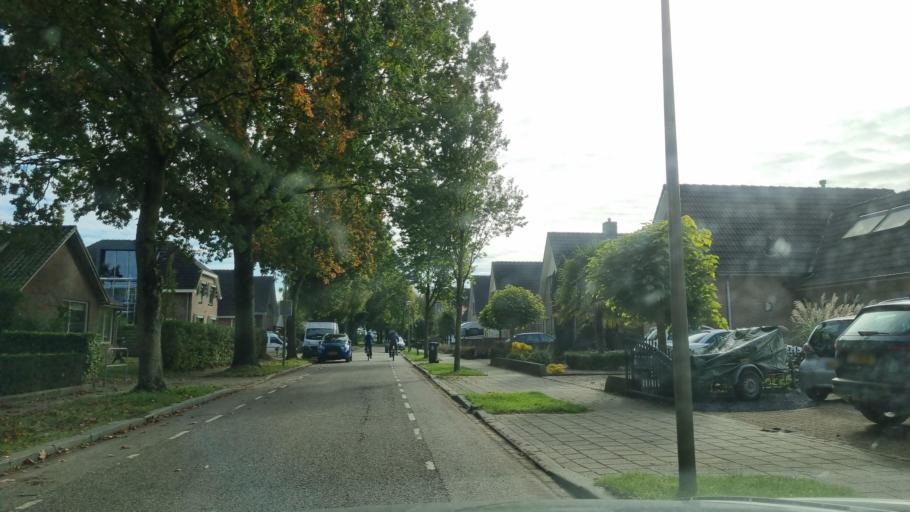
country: NL
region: Gelderland
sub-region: Gemeente Zevenaar
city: Zevenaar
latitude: 51.8615
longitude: 6.0408
